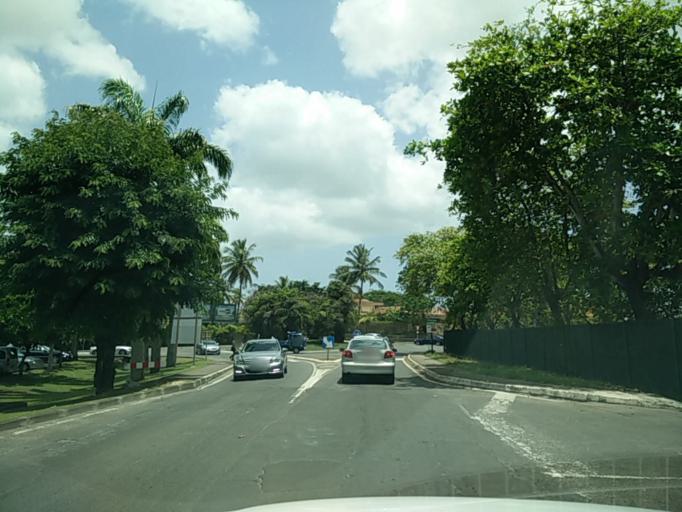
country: GP
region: Guadeloupe
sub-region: Guadeloupe
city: Les Abymes
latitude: 16.2595
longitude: -61.5178
